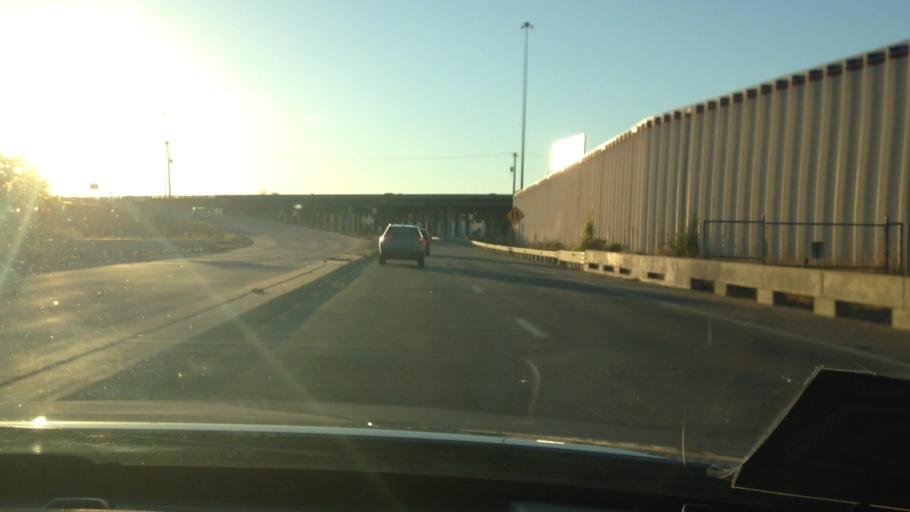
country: US
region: Kansas
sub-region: Johnson County
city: Westwood
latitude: 39.0578
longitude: -94.6259
